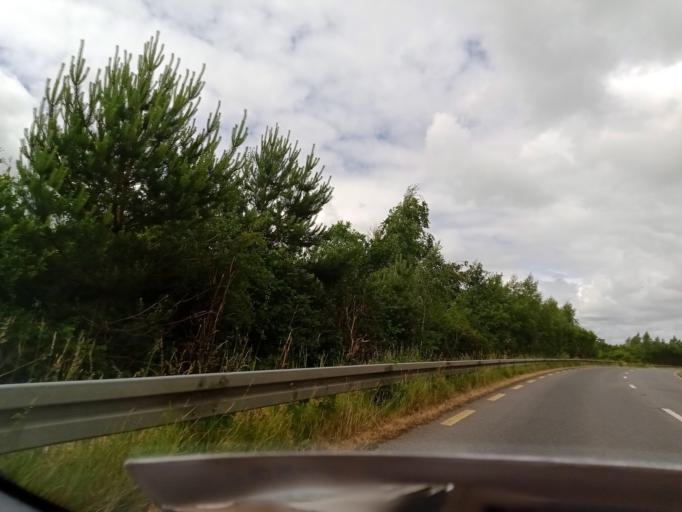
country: IE
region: Leinster
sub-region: Kilkenny
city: Thomastown
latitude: 52.4849
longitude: -7.2214
